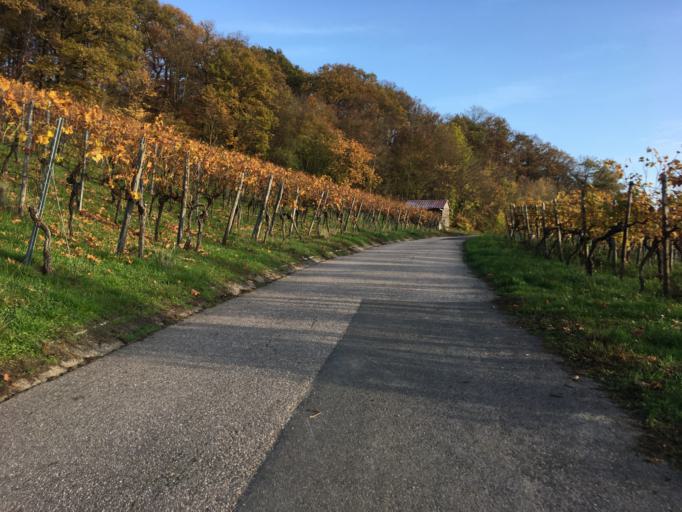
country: DE
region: Baden-Wuerttemberg
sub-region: Regierungsbezirk Stuttgart
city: Erlenbach
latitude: 49.1480
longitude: 9.2539
